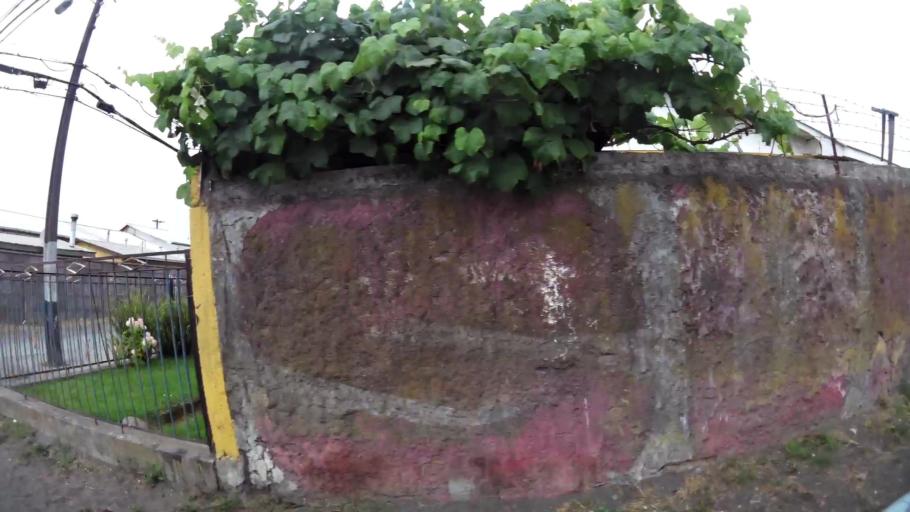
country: CL
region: Biobio
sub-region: Provincia de Concepcion
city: Concepcion
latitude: -36.8013
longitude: -73.0803
